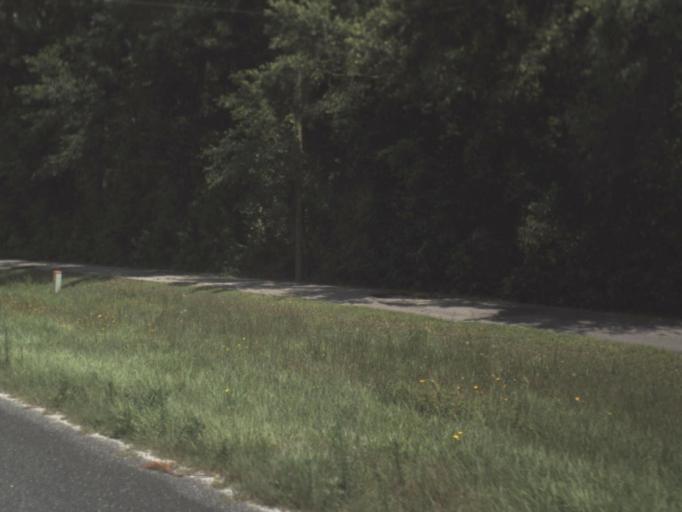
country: US
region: Florida
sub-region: Suwannee County
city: Wellborn
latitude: 29.9524
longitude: -82.8578
